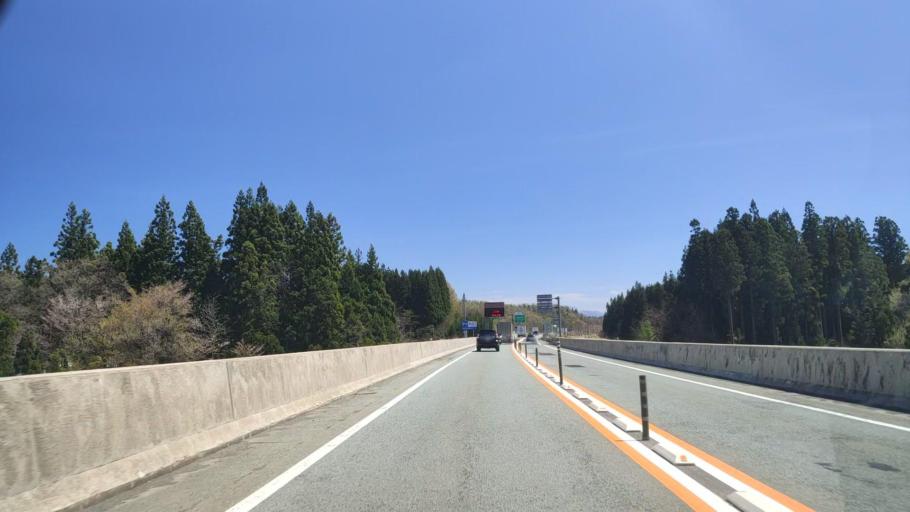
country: JP
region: Yamagata
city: Obanazawa
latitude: 38.6629
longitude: 140.3587
